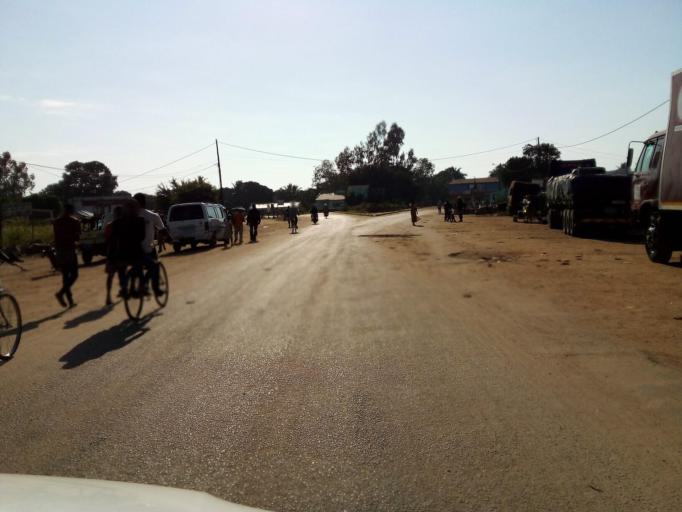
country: MZ
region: Zambezia
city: Quelimane
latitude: -17.5954
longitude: 36.8138
